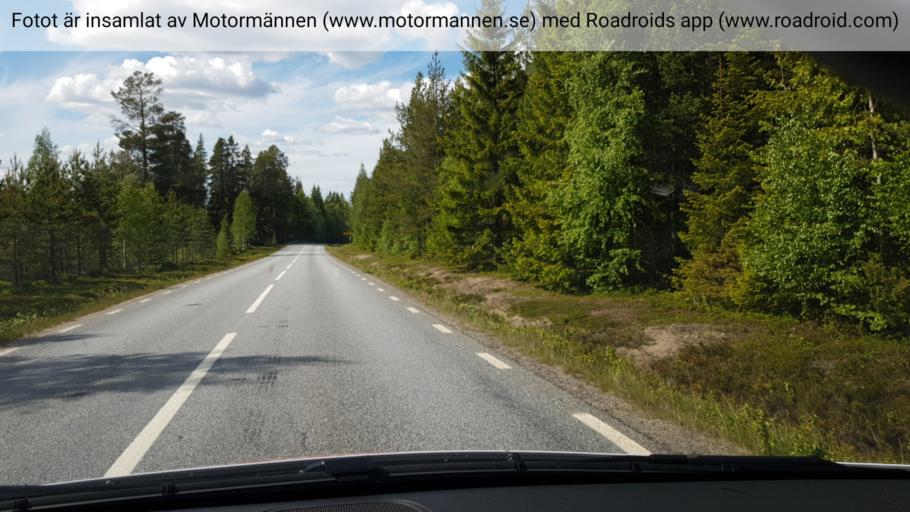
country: SE
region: Vaesterbotten
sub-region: Skelleftea Kommun
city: Burtraesk
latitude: 64.5070
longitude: 20.5007
